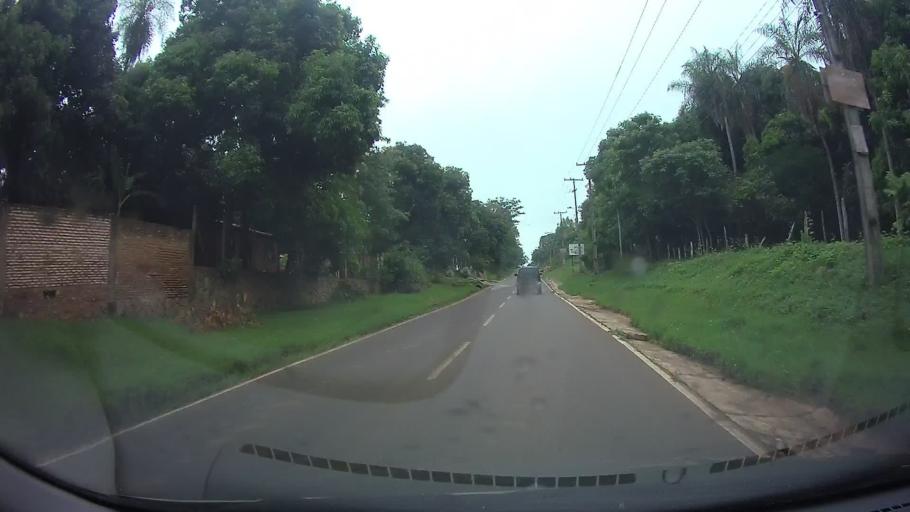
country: PY
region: Central
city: Itaugua
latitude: -25.3690
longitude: -57.3473
